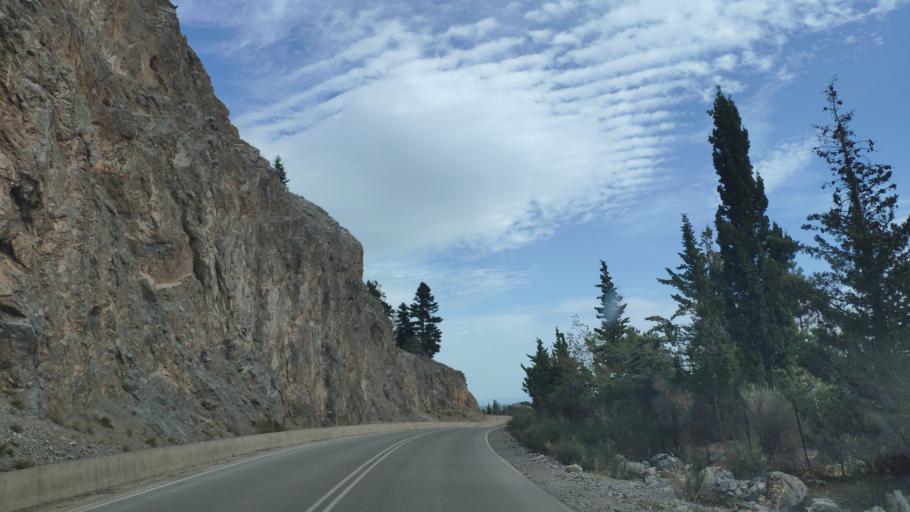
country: GR
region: Central Greece
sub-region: Nomos Fokidos
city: Amfissa
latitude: 38.6551
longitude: 22.3815
